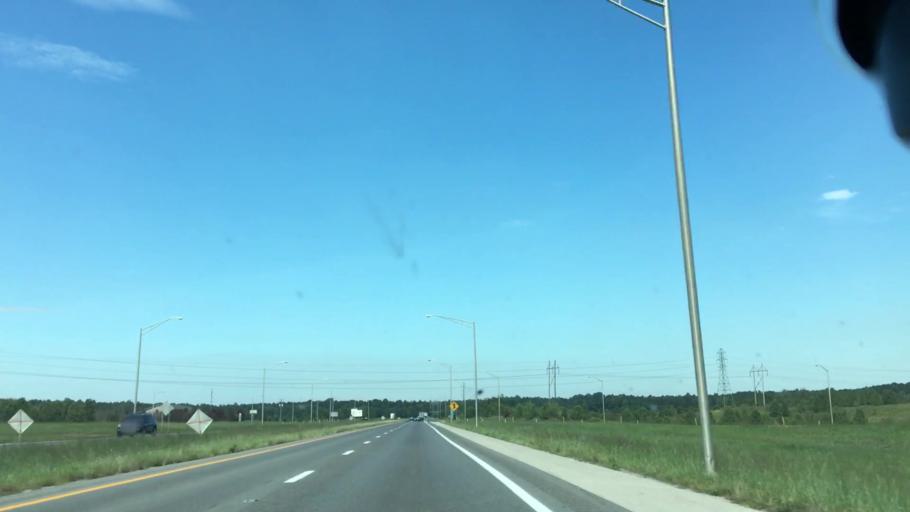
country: US
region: Kentucky
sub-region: Hopkins County
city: Madisonville
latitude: 37.2950
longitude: -87.4621
